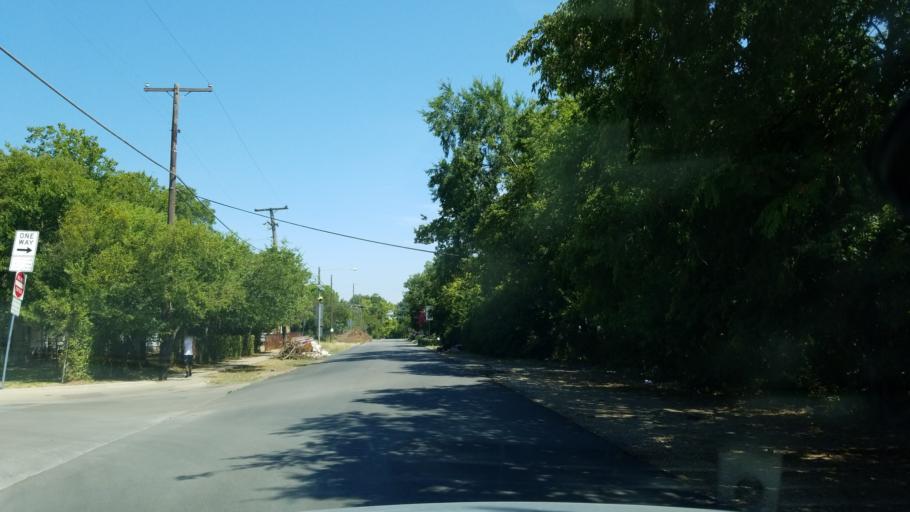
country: US
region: Texas
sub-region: Dallas County
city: Cockrell Hill
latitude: 32.7435
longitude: -96.8831
